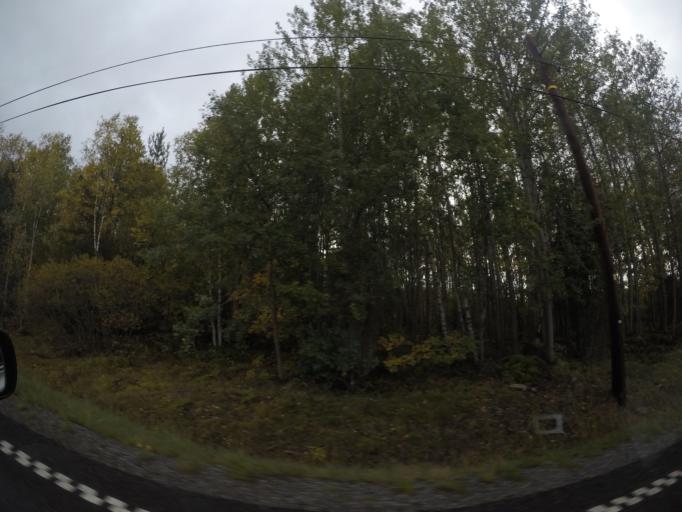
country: SE
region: Soedermanland
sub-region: Eskilstuna Kommun
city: Kvicksund
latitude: 59.3181
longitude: 16.3054
